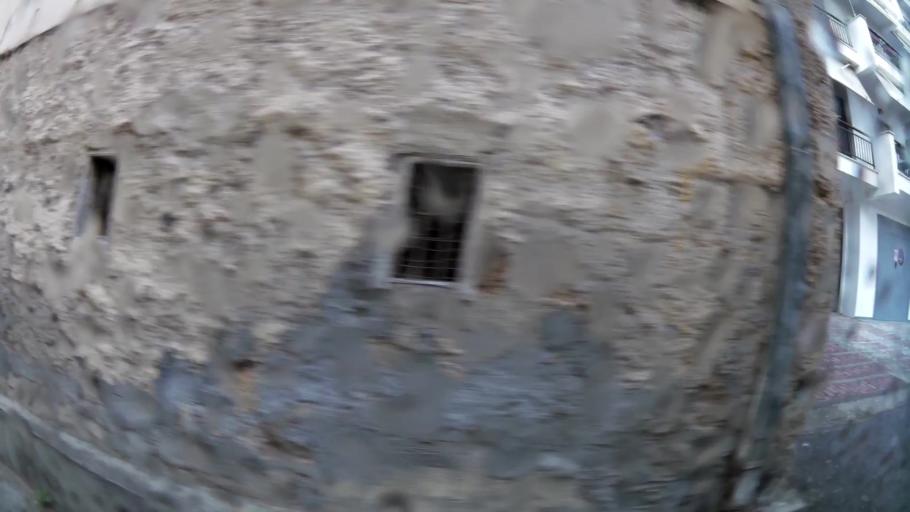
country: GR
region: Central Macedonia
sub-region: Nomos Imathias
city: Veroia
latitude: 40.5226
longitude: 22.1980
